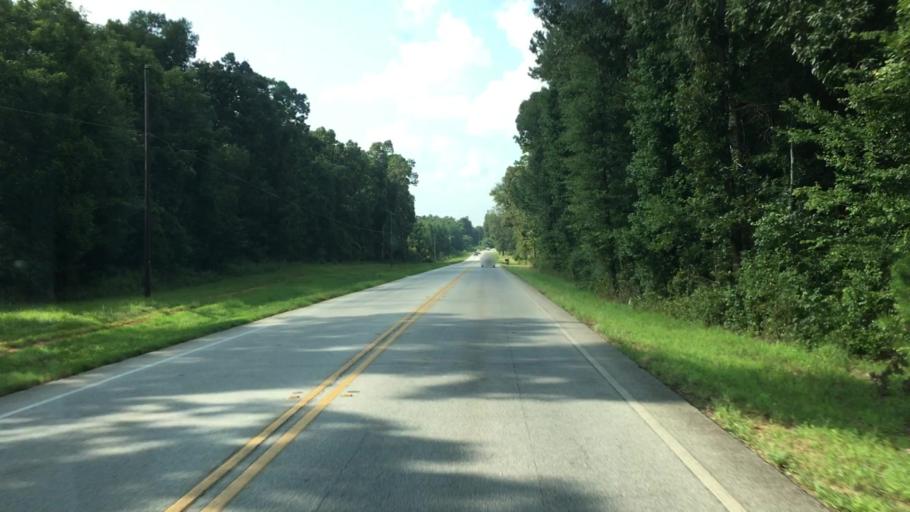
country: US
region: Georgia
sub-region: Walton County
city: Social Circle
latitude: 33.5799
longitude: -83.7448
